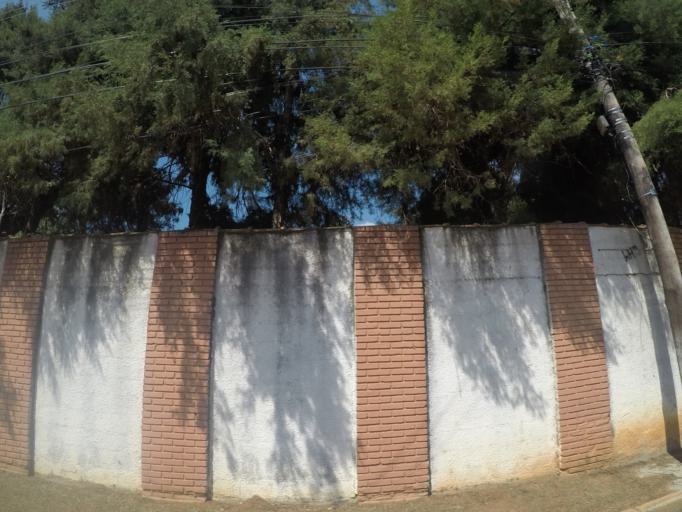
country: BR
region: Sao Paulo
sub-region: Cabreuva
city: Cabreuva
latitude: -23.2523
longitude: -47.0627
